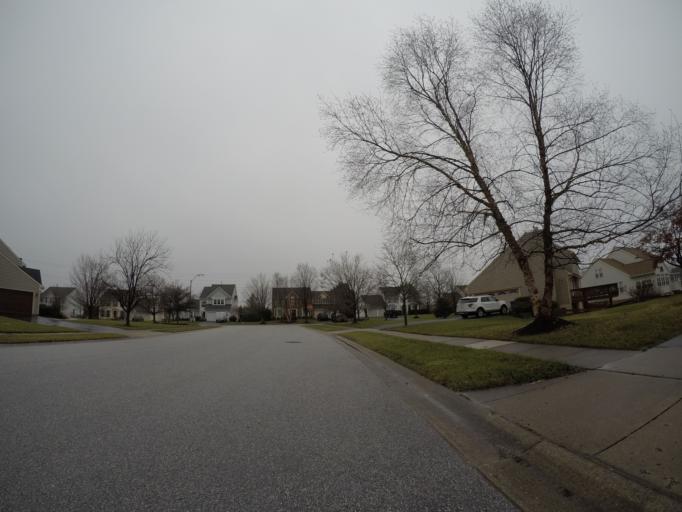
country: US
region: Maryland
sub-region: Howard County
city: Ilchester
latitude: 39.2244
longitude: -76.7937
